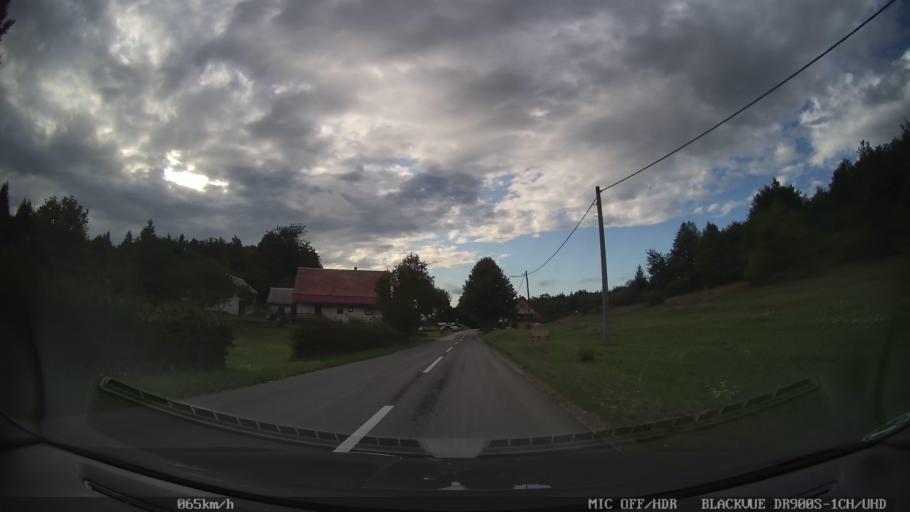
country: HR
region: Licko-Senjska
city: Jezerce
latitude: 44.9647
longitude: 15.5222
